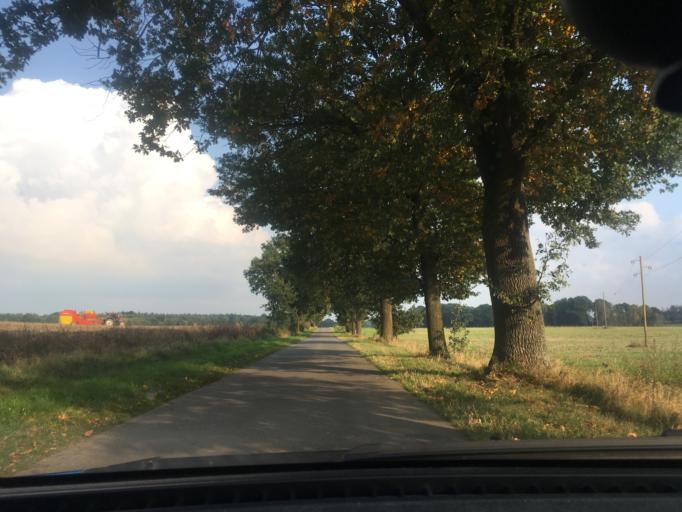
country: DE
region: Lower Saxony
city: Vastorf
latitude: 53.2042
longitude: 10.5623
